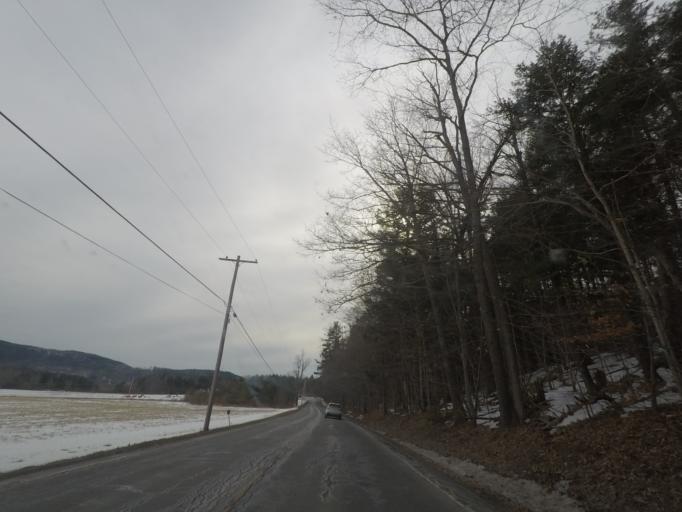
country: US
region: New York
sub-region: Albany County
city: Altamont
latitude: 42.6449
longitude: -74.1372
